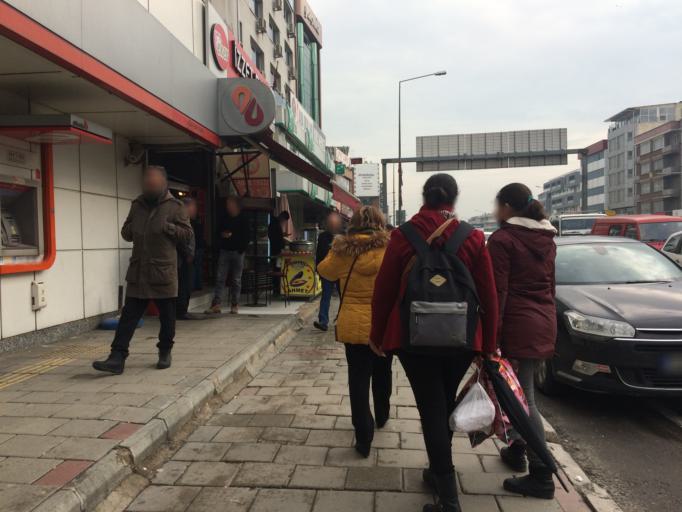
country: TR
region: Izmir
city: Karsiyaka
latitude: 38.4916
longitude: 27.0658
